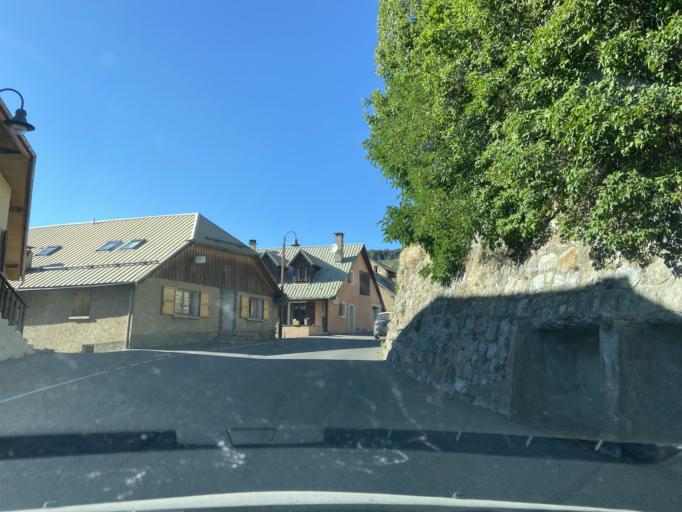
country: FR
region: Provence-Alpes-Cote d'Azur
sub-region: Departement des Hautes-Alpes
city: Guillestre
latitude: 44.6083
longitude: 6.6884
